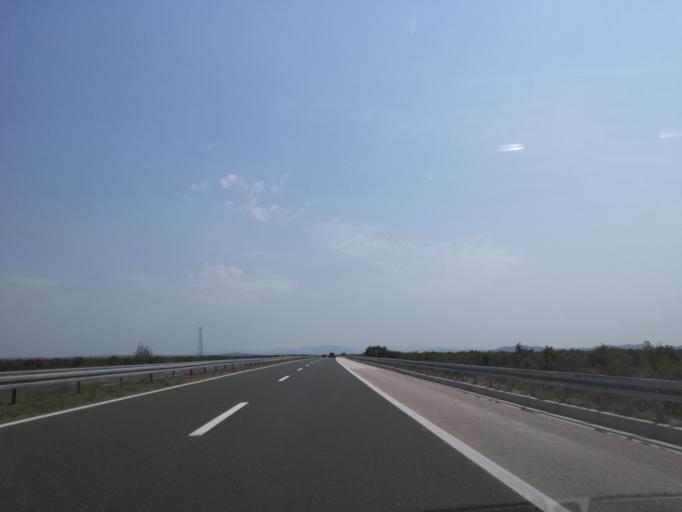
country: HR
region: Sibensko-Kniniska
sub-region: Grad Sibenik
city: Pirovac
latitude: 43.9159
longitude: 15.7454
